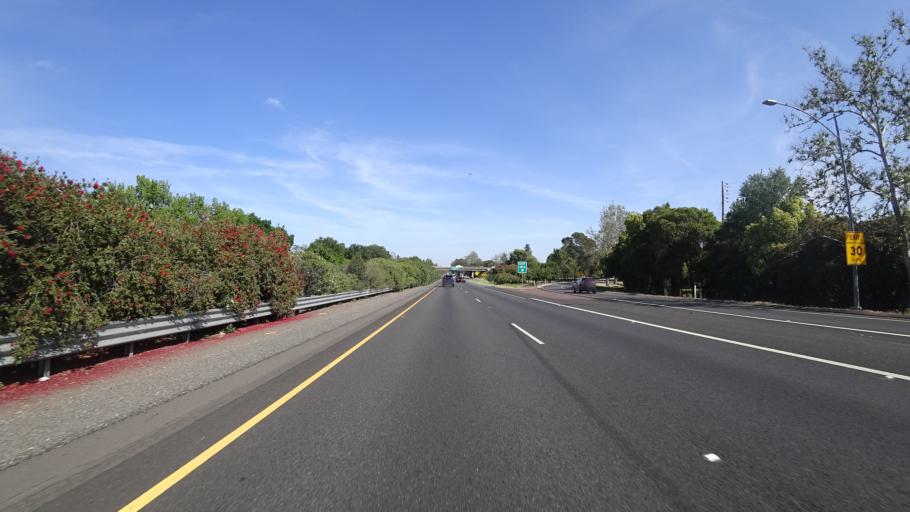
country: US
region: California
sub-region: Butte County
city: Chico
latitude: 39.7554
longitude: -121.8475
